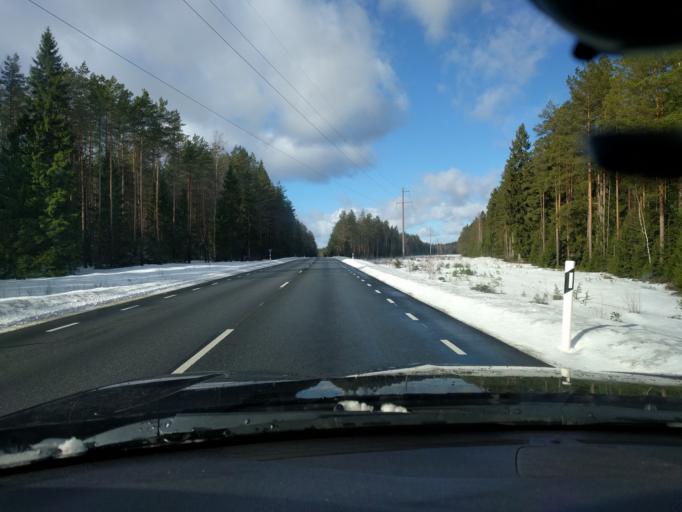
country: EE
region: Harju
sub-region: Kuusalu vald
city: Kuusalu
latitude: 59.2072
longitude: 25.5609
